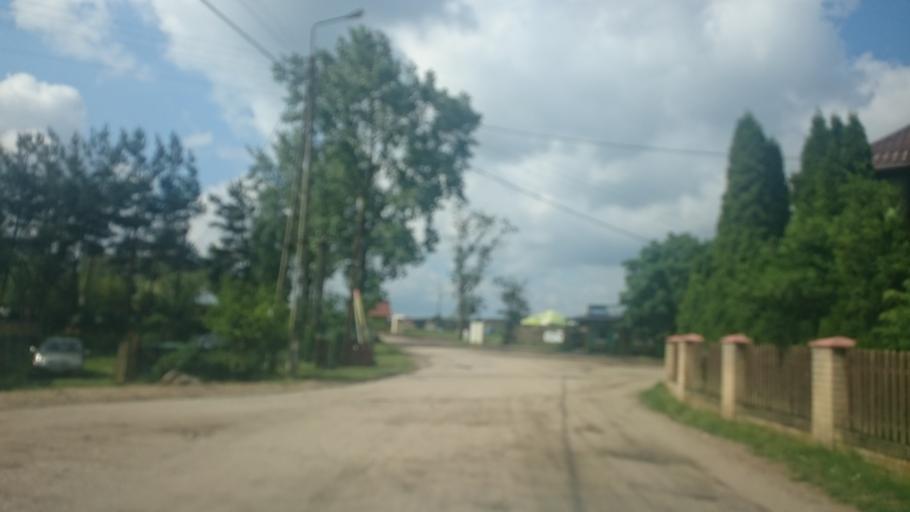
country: PL
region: Pomeranian Voivodeship
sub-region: Powiat koscierski
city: Karsin
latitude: 53.9745
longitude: 17.9285
